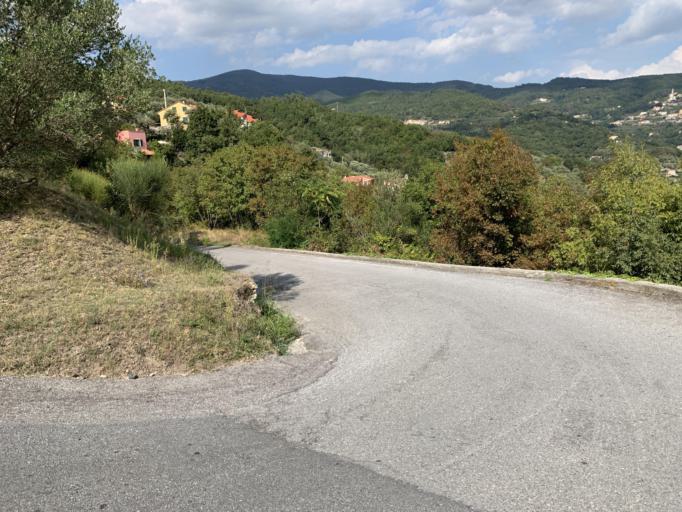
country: IT
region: Liguria
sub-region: Provincia di Savona
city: Calice Ligure
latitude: 44.2002
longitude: 8.2861
